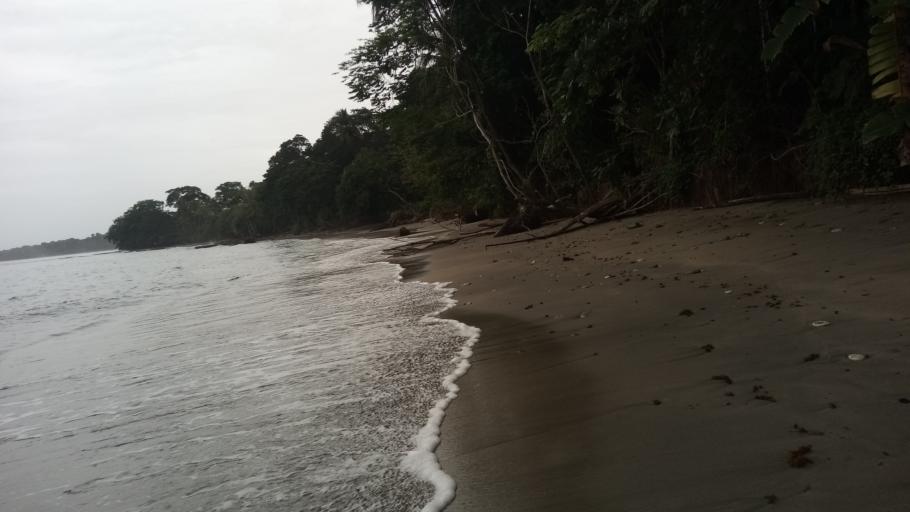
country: CR
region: Limon
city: Sixaola
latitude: 9.6282
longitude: -82.6199
